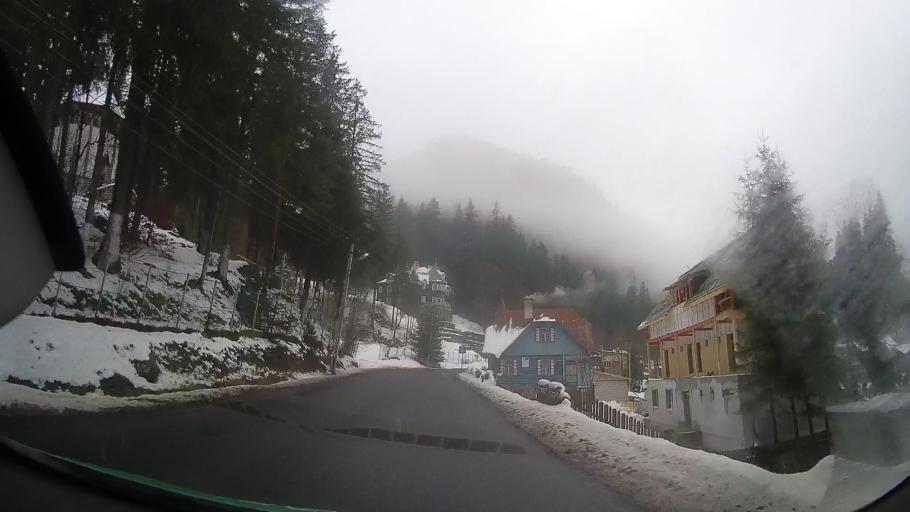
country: RO
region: Neamt
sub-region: Comuna Bicaz Chei
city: Bicaz Chei
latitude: 46.7959
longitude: 25.8013
